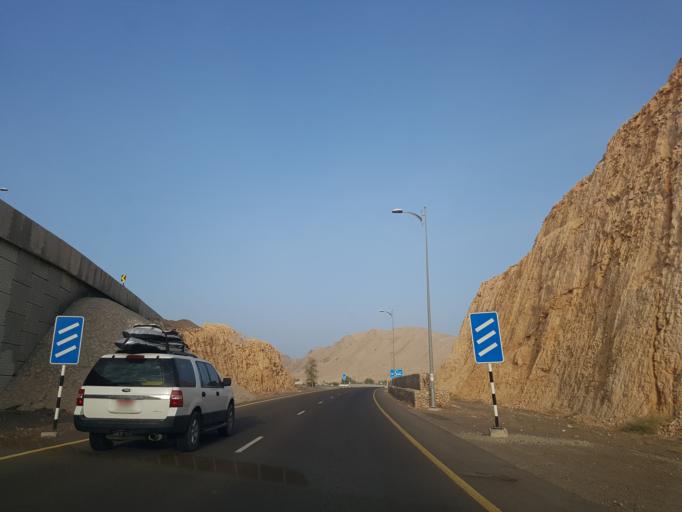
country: OM
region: Al Buraimi
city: Al Buraymi
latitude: 24.2310
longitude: 55.9539
